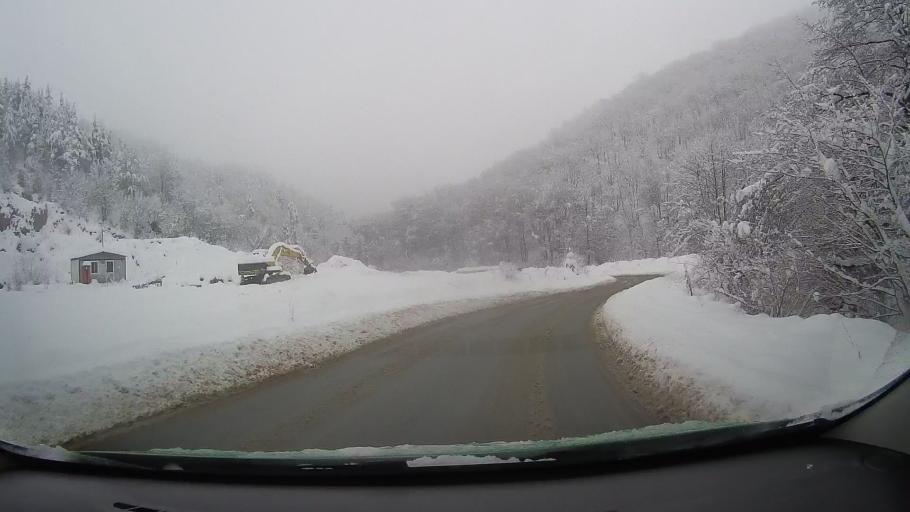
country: RO
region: Sibiu
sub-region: Comuna Tilisca
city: Tilisca
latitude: 45.8025
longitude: 23.8100
